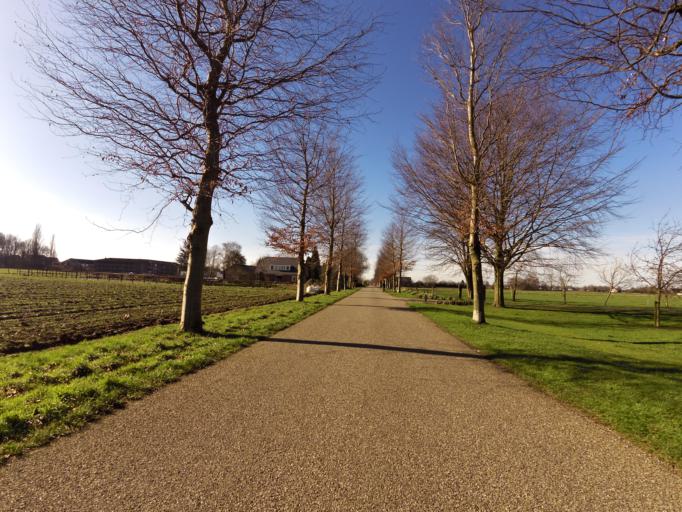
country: NL
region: Gelderland
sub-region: Gemeente Doesburg
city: Doesburg
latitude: 51.9416
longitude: 6.1519
